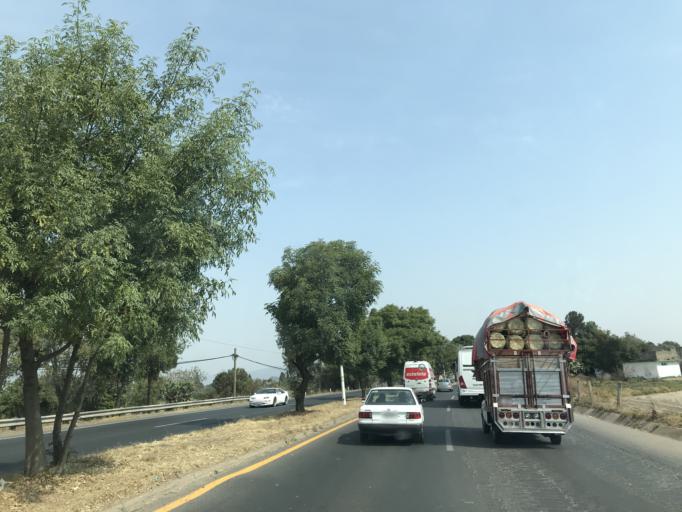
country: MX
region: Tlaxcala
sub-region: Teolocholco
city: Teolocholco
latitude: 19.2561
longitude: -98.1999
